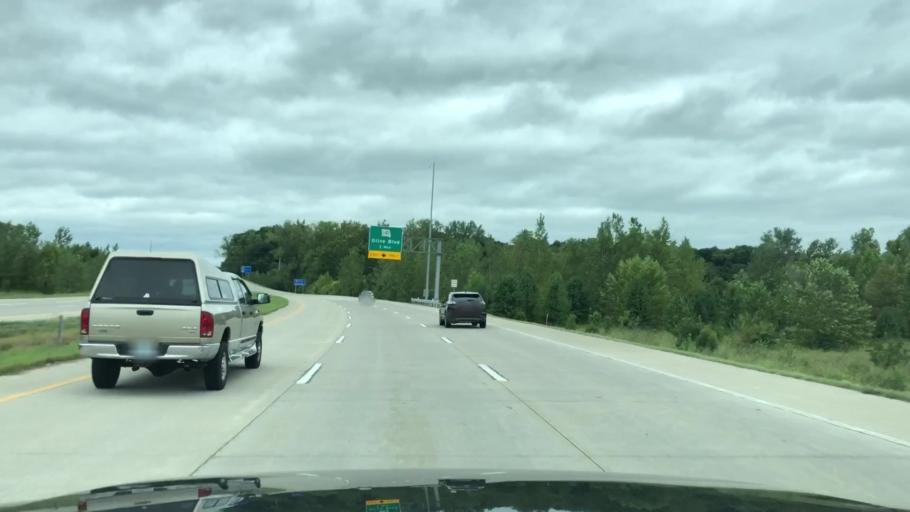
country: US
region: Missouri
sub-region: Saint Louis County
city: Maryland Heights
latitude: 38.6969
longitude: -90.5029
